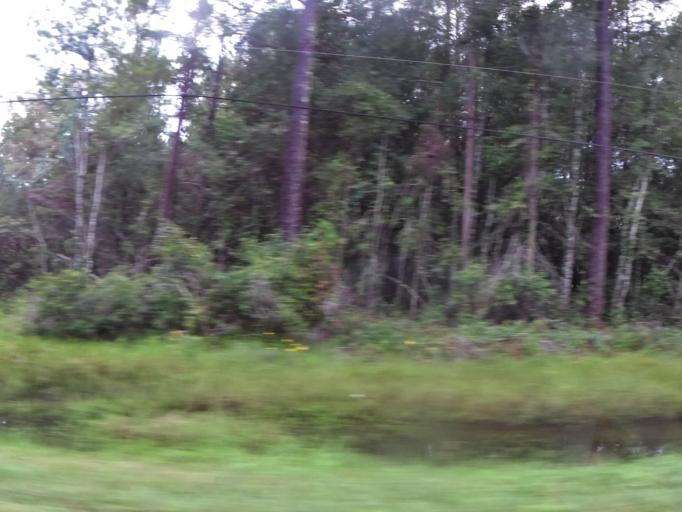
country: US
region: Florida
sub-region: Duval County
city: Baldwin
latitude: 30.3948
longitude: -81.9470
